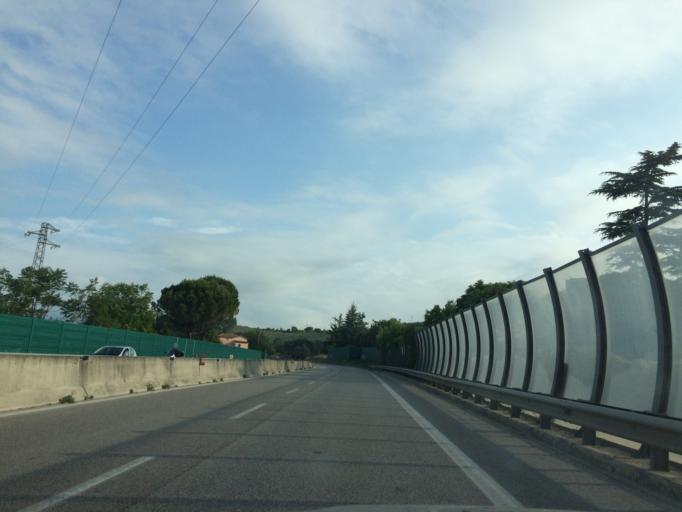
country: IT
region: Umbria
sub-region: Provincia di Perugia
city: Trevi
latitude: 42.9276
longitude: 12.7285
